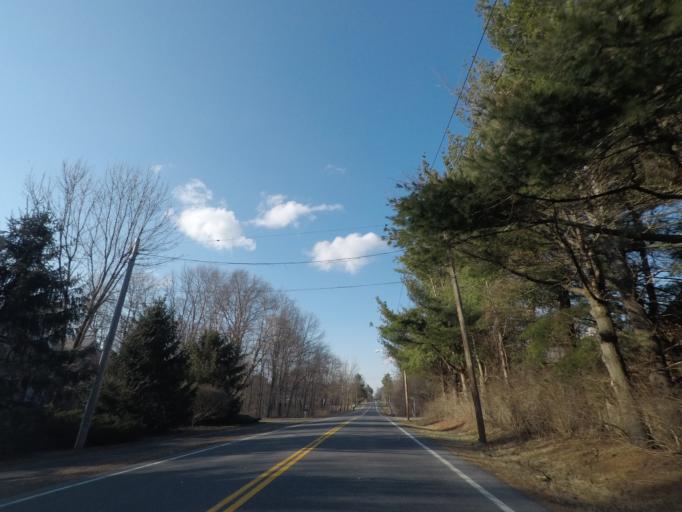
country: US
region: New York
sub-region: Schenectady County
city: Niskayuna
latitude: 42.8354
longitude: -73.7941
